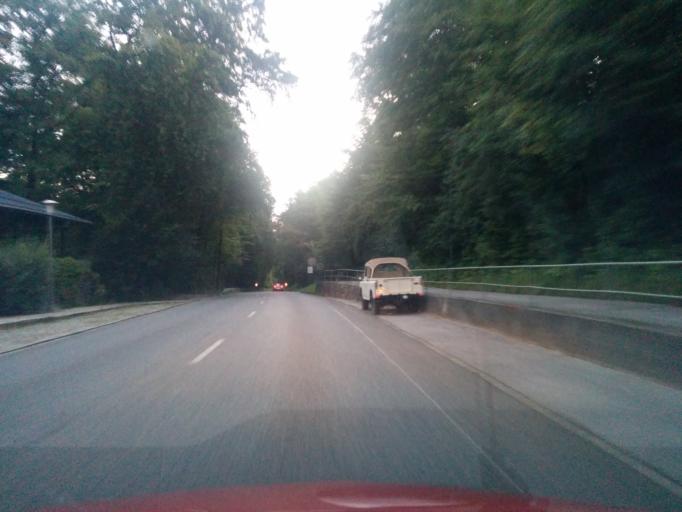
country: DE
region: Bavaria
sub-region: Upper Bavaria
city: Starnberg
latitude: 47.9935
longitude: 11.3347
